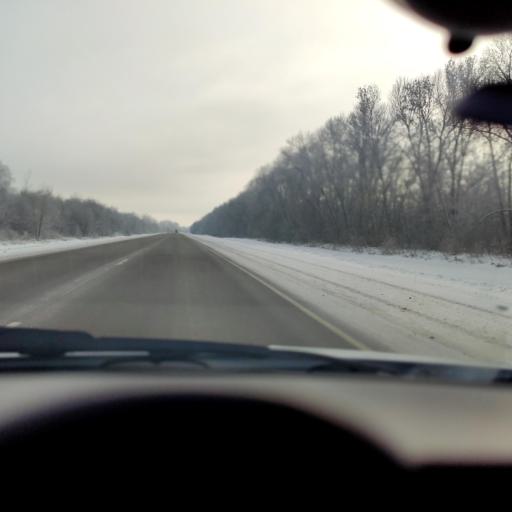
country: RU
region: Kursk
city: Kirovskiy
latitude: 51.6814
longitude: 36.5745
